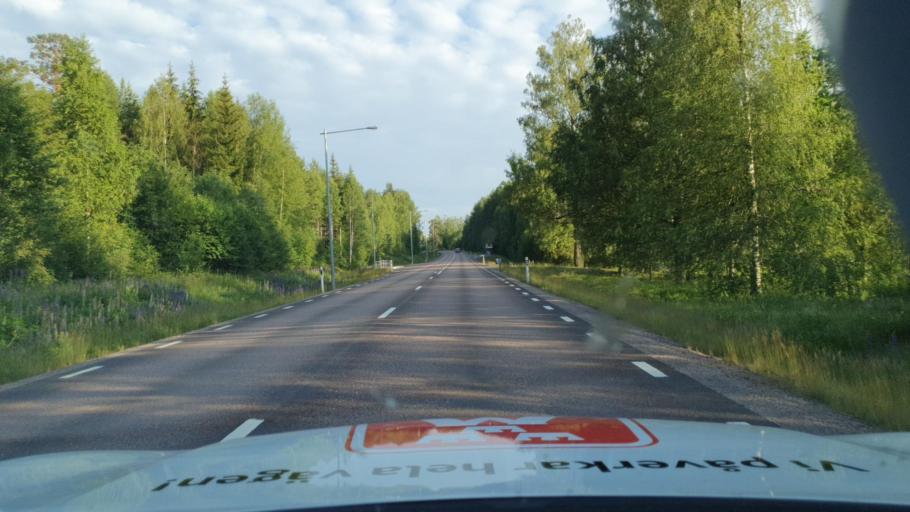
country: SE
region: Vaermland
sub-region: Hagfors Kommun
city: Hagfors
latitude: 59.9679
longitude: 13.6579
